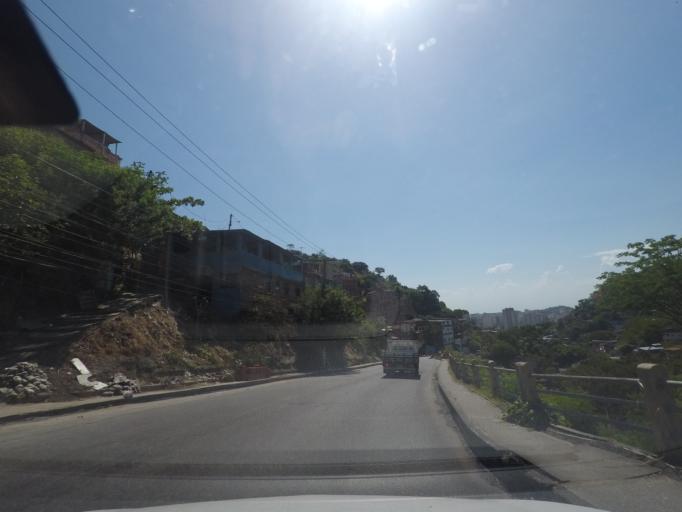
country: BR
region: Rio de Janeiro
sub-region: Niteroi
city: Niteroi
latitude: -22.9065
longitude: -43.0790
